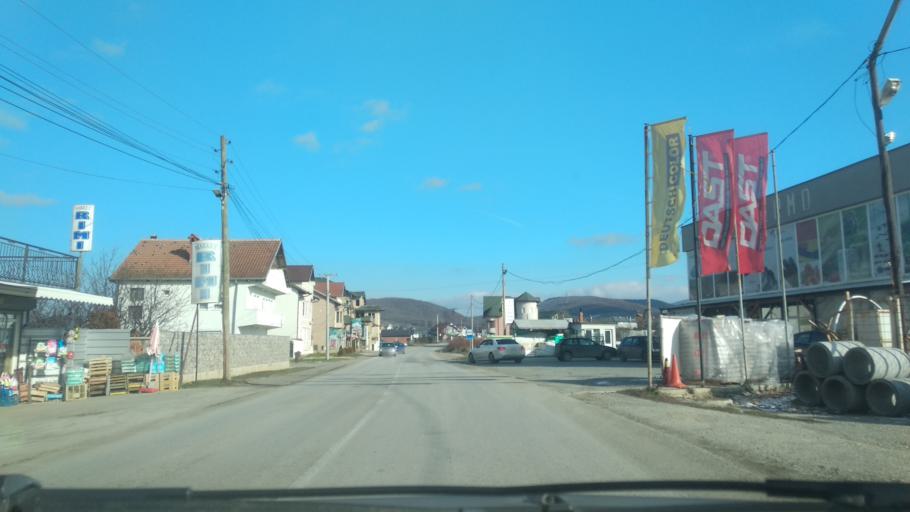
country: XK
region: Pristina
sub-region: Komuna e Prishtines
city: Pristina
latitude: 42.7447
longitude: 21.1328
